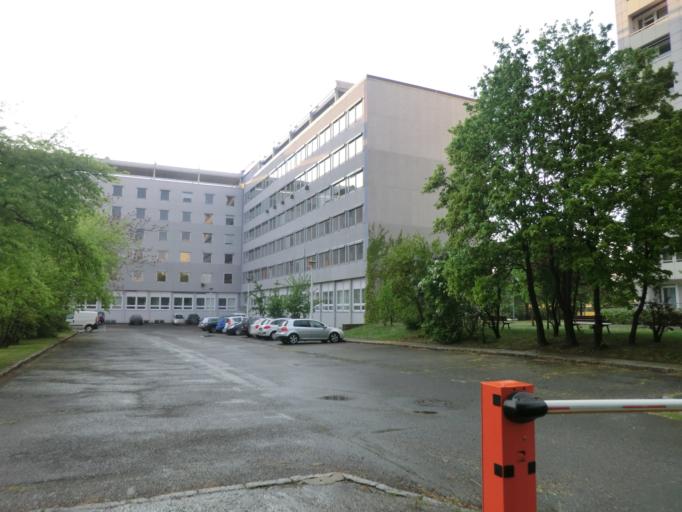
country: DE
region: Saxony
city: Dresden
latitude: 51.0478
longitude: 13.7466
